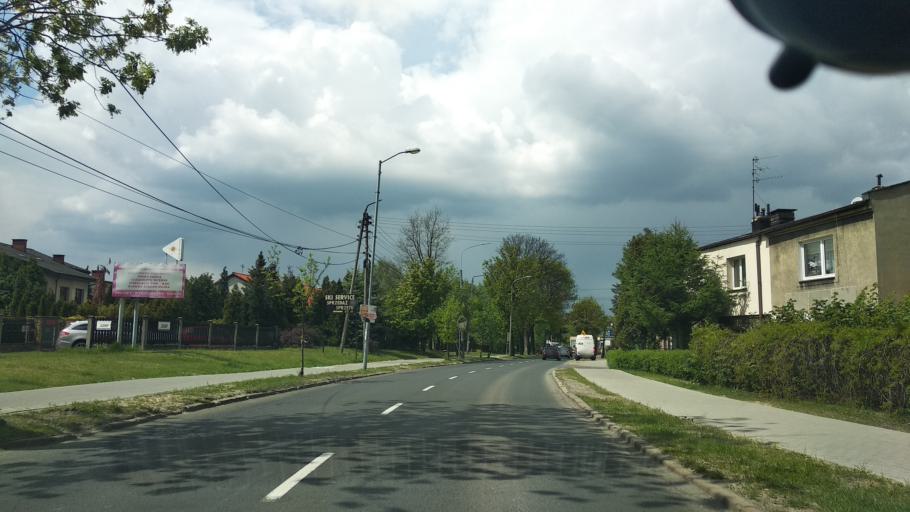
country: PL
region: Silesian Voivodeship
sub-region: Swietochlowice
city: Swietochlowice
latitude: 50.2297
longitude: 18.9547
